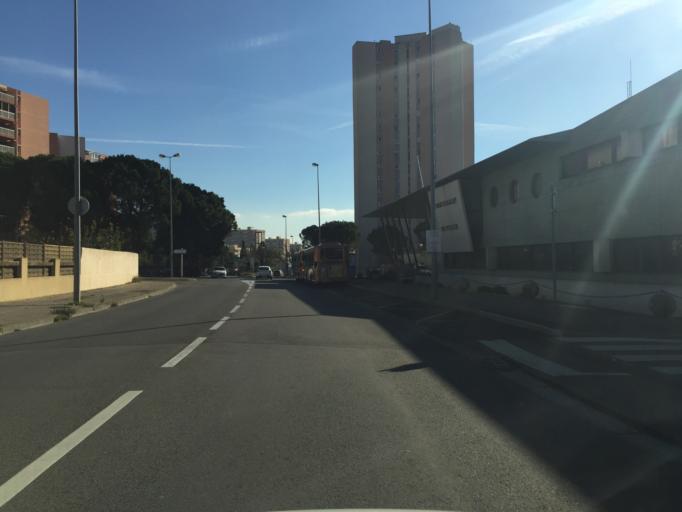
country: FR
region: Provence-Alpes-Cote d'Azur
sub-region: Departement des Bouches-du-Rhone
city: Salon-de-Provence
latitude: 43.6547
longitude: 5.0979
